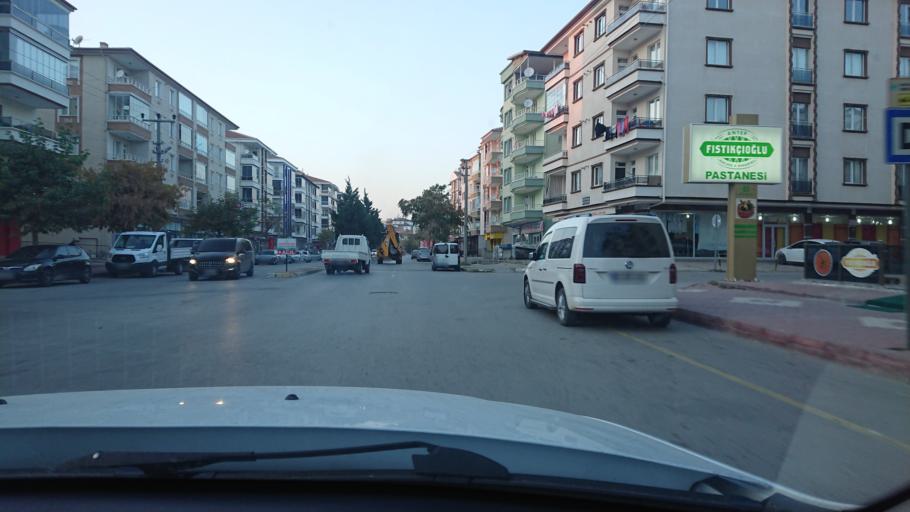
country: TR
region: Aksaray
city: Aksaray
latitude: 38.3607
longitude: 34.0377
